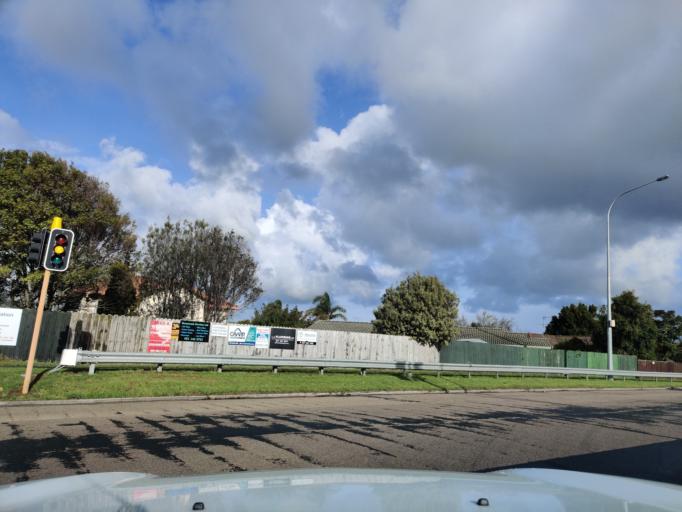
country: NZ
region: Auckland
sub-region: Auckland
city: Pakuranga
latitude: -36.9162
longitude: 174.9145
